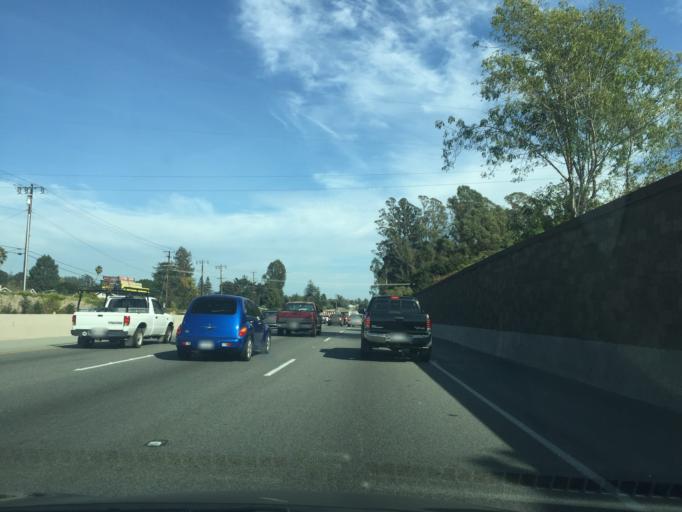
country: US
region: California
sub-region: Santa Cruz County
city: Live Oak
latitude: 36.9881
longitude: -121.9990
